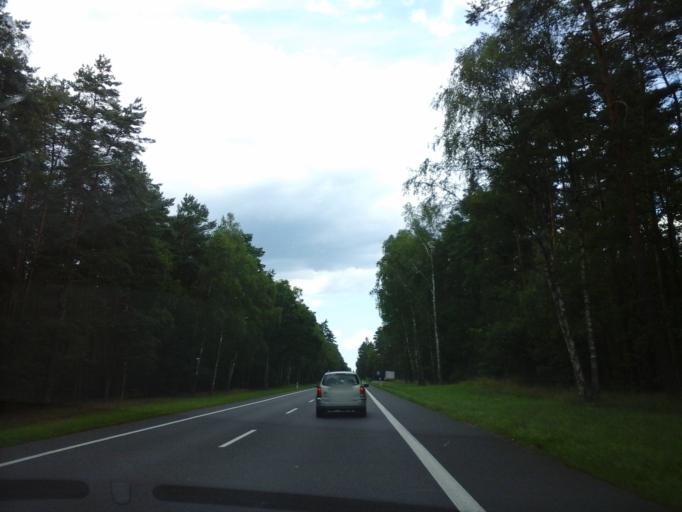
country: PL
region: West Pomeranian Voivodeship
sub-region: Powiat goleniowski
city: Goleniow
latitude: 53.6523
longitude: 14.8161
